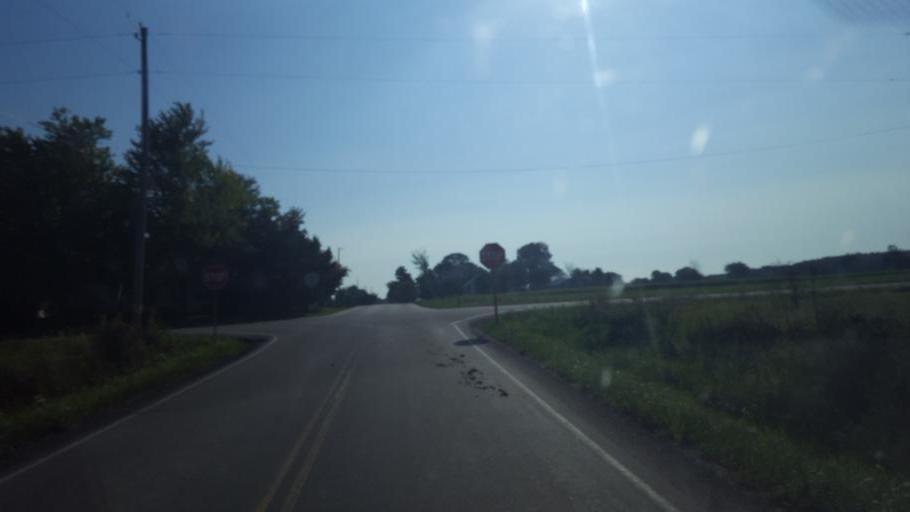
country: US
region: Ohio
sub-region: Portage County
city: Hiram
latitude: 41.3869
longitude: -81.1087
